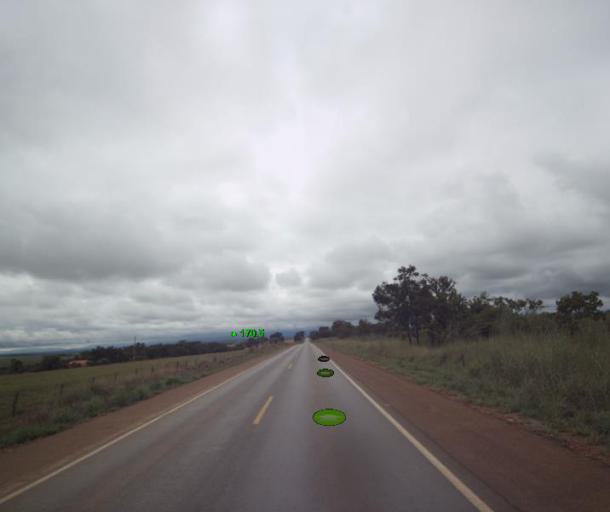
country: BR
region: Goias
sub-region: Uruacu
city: Uruacu
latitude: -14.7024
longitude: -49.1057
